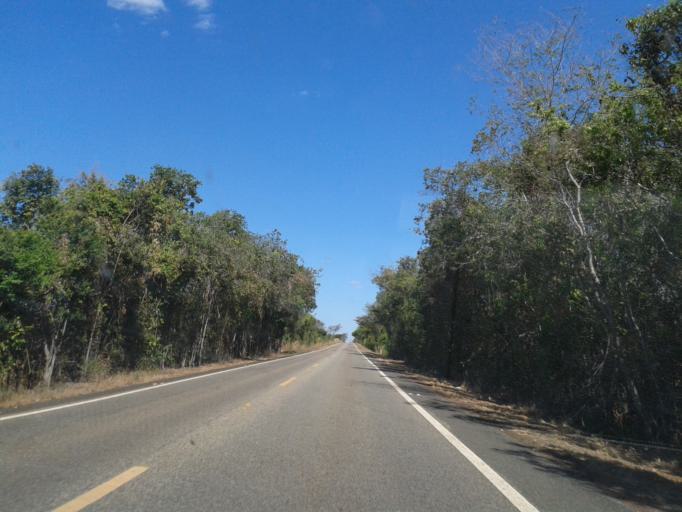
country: BR
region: Goias
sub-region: Sao Miguel Do Araguaia
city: Sao Miguel do Araguaia
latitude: -13.4818
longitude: -50.3059
